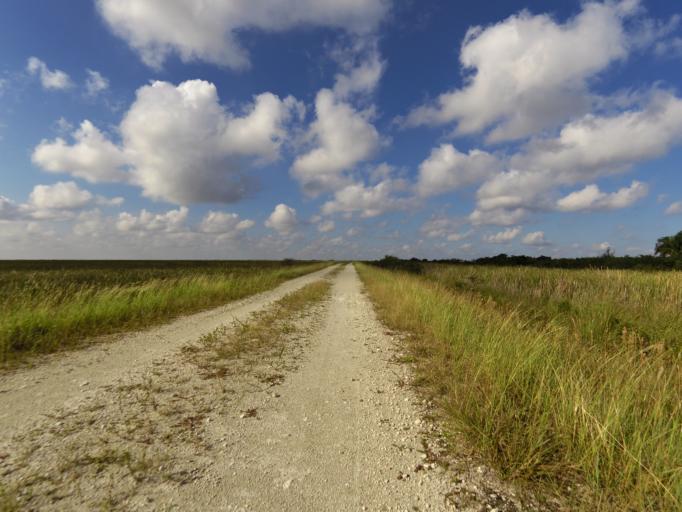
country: US
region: Florida
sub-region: Broward County
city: Weston
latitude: 26.0514
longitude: -80.4707
